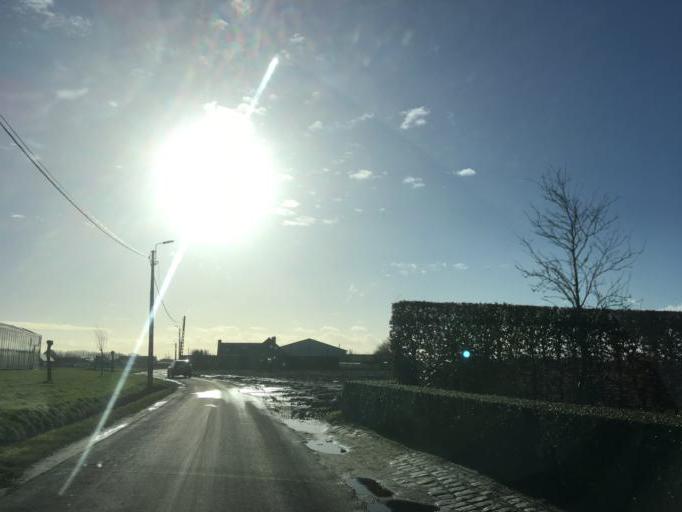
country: BE
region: Flanders
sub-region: Provincie West-Vlaanderen
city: Ardooie
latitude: 50.9829
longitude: 3.1733
